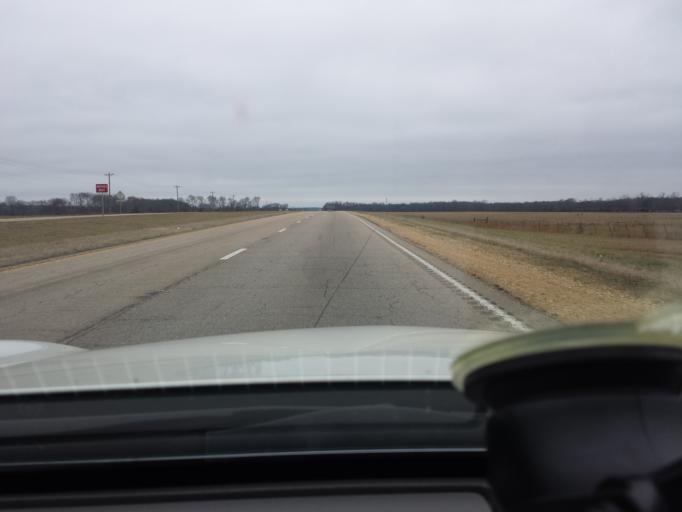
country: US
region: Mississippi
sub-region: Chickasaw County
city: Okolona
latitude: 34.0364
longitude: -88.7027
